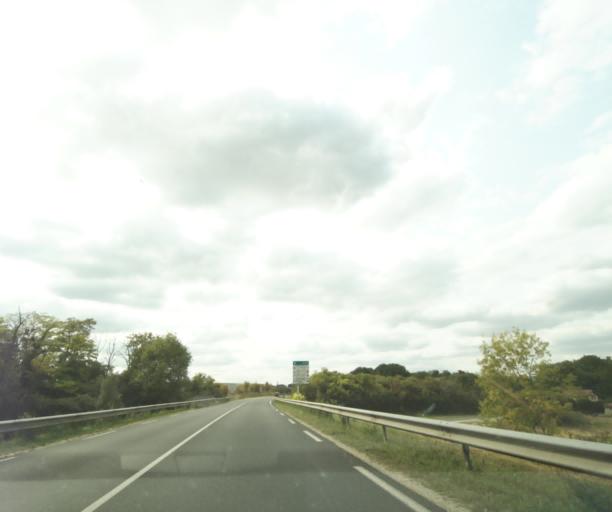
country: FR
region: Centre
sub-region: Departement de l'Indre
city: Buzancais
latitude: 46.8782
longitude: 1.4201
